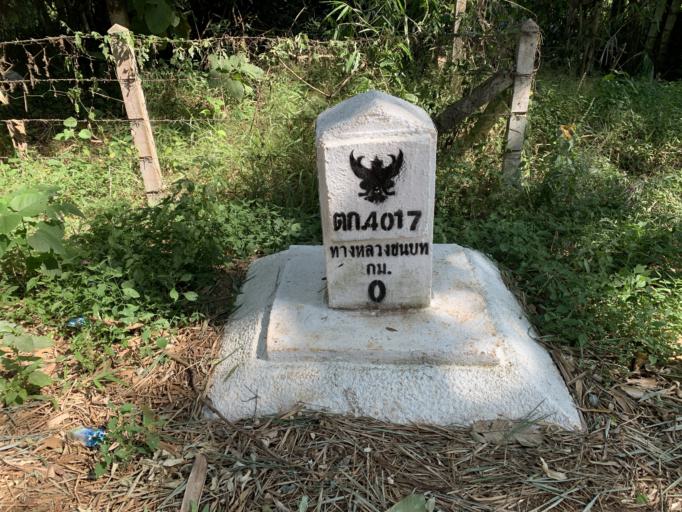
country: TH
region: Tak
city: Phop Phra
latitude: 16.4878
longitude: 98.7868
